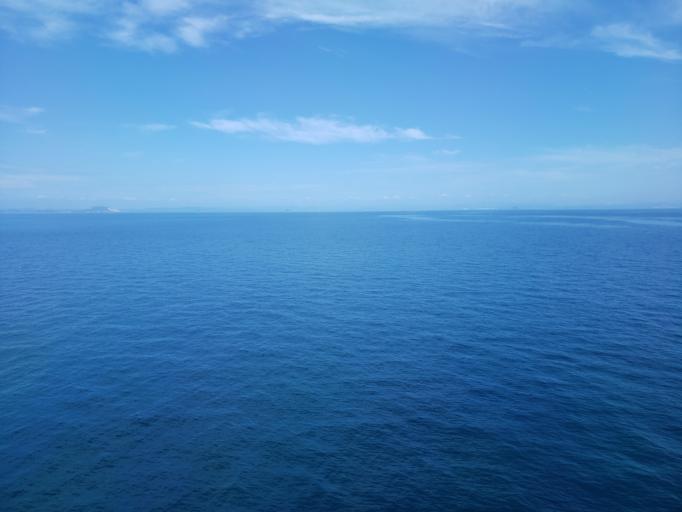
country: JP
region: Hyogo
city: Shirahamacho-usazakiminami
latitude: 34.5475
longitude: 134.7262
